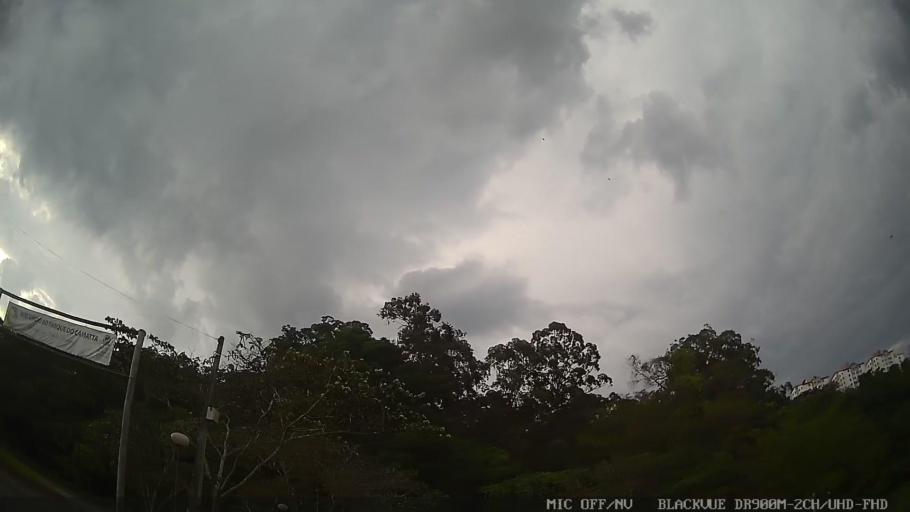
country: BR
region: Sao Paulo
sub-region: Itatiba
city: Itatiba
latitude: -23.0266
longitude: -46.8466
